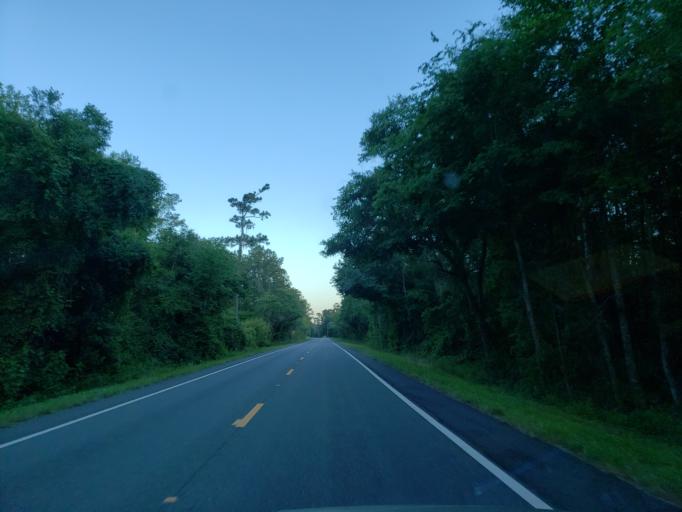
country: US
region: Georgia
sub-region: Echols County
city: Statenville
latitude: 30.5780
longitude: -83.1678
